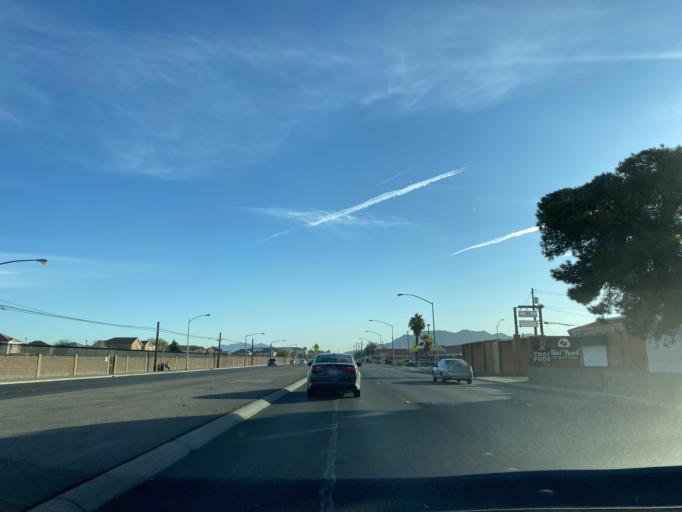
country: US
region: Nevada
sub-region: Clark County
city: Nellis Air Force Base
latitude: 36.2403
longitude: -115.0677
